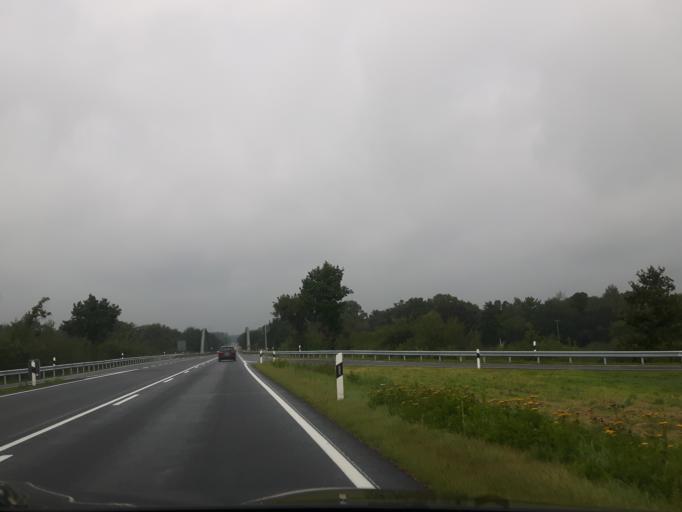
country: DE
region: Lower Saxony
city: Lingen
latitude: 52.4937
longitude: 7.2996
